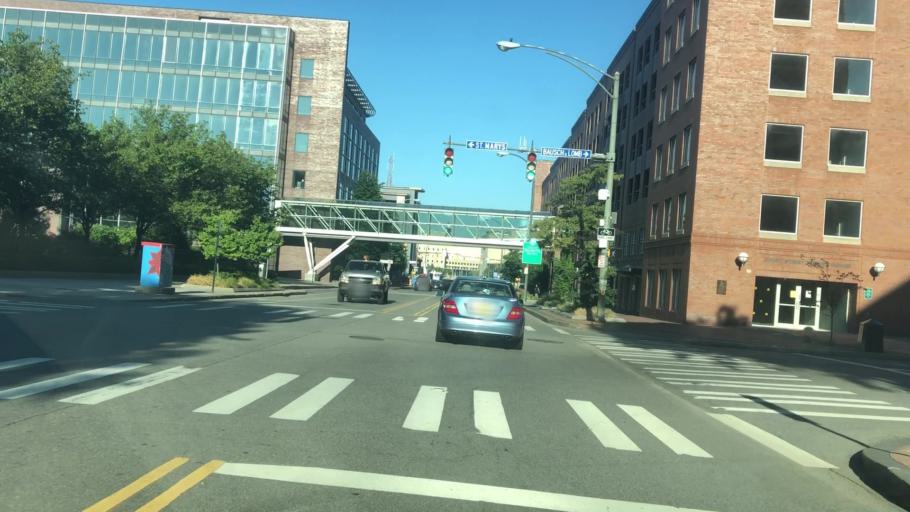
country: US
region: New York
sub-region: Monroe County
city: Rochester
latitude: 43.1541
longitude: -77.6057
